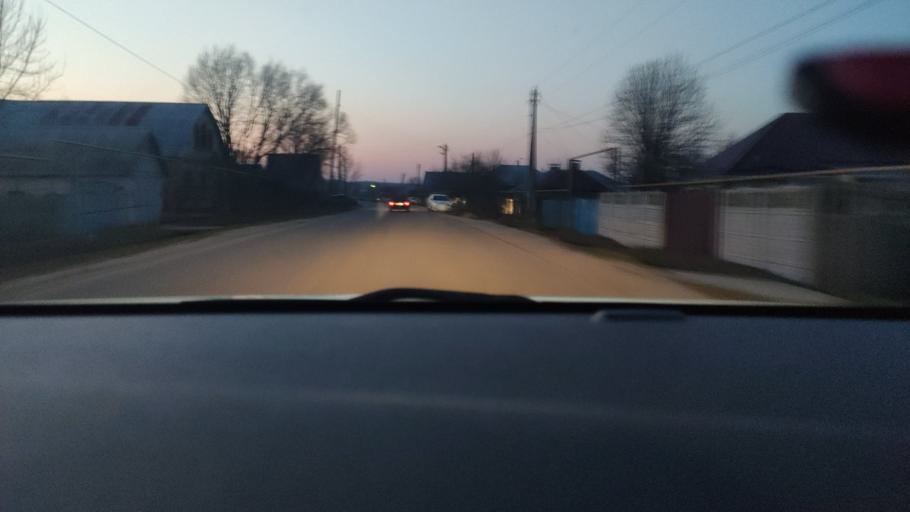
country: RU
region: Voronezj
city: Shilovo
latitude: 51.4832
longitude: 39.0181
